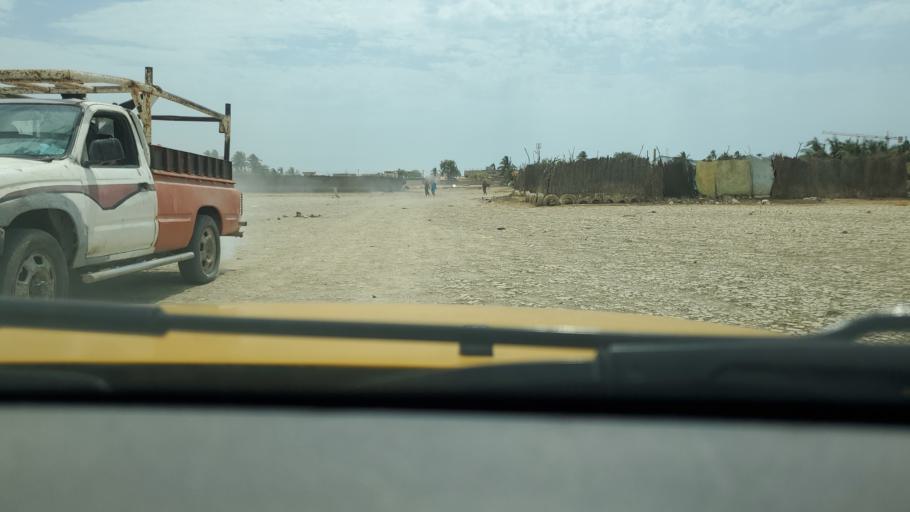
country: SN
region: Saint-Louis
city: Saint-Louis
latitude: 16.0261
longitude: -16.4707
